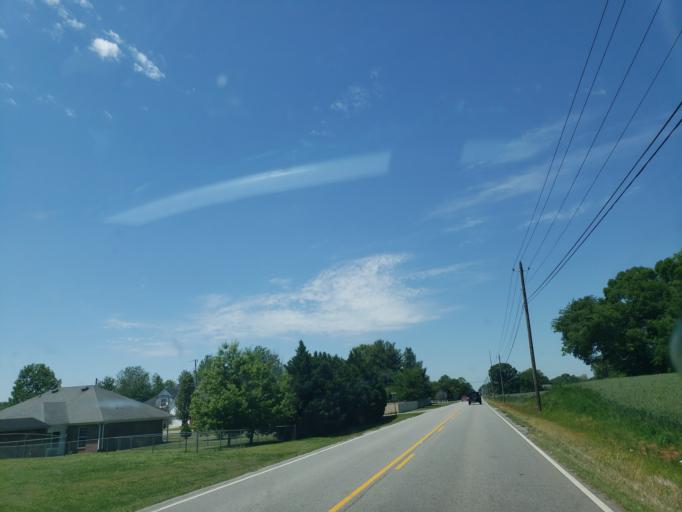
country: US
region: Alabama
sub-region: Madison County
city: Hazel Green
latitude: 34.9322
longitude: -86.5401
